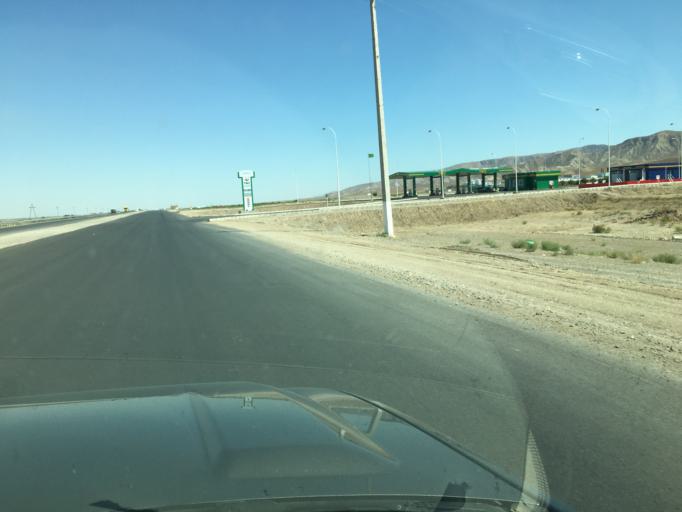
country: TM
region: Balkan
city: Serdar
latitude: 38.9751
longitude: 56.3162
